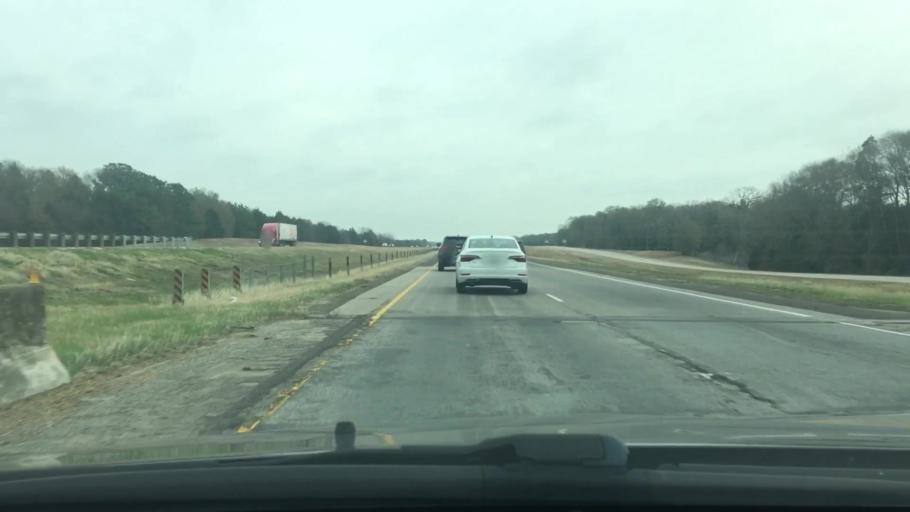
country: US
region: Texas
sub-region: Freestone County
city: Fairfield
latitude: 31.7493
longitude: -96.1989
